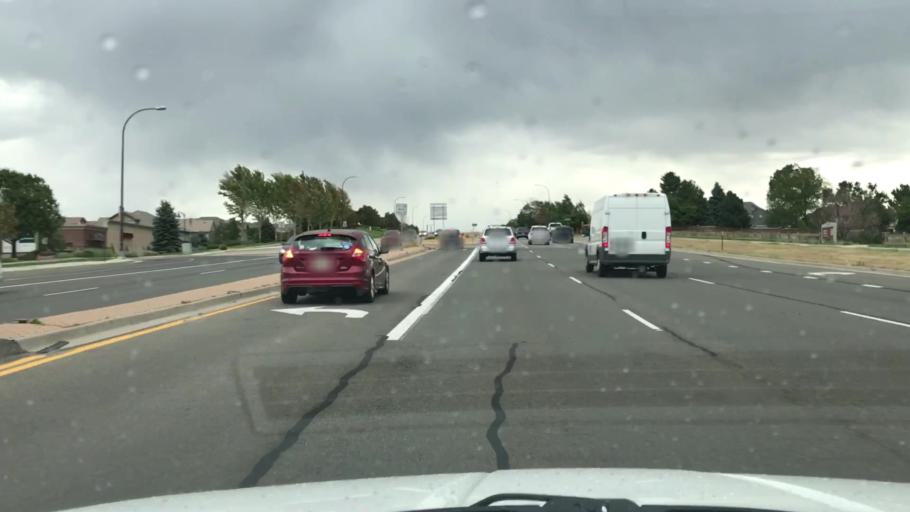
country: US
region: Colorado
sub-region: Adams County
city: Northglenn
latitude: 39.9141
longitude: -105.0221
